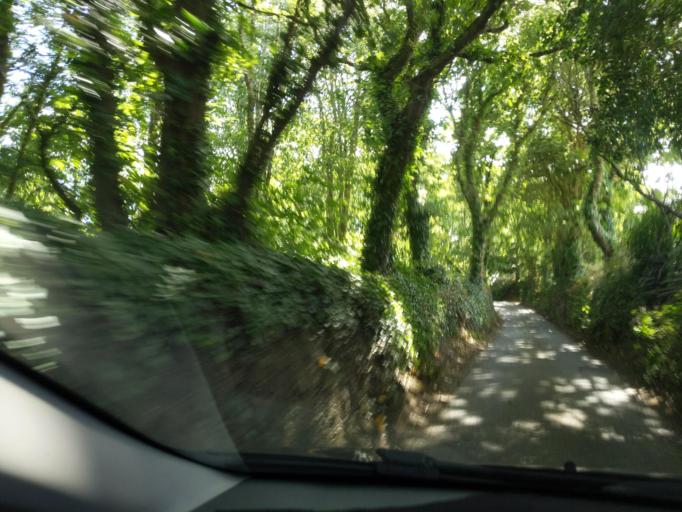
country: GB
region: England
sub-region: Cornwall
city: Torpoint
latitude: 50.3642
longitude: -4.2373
